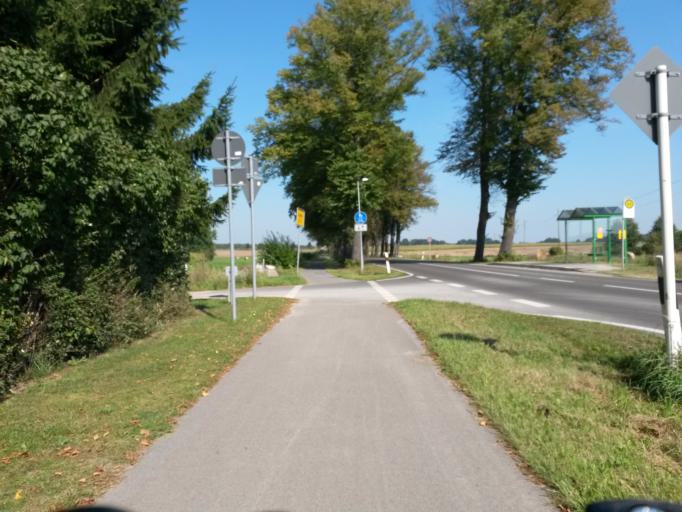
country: DE
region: Brandenburg
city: Templin
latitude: 53.0831
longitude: 13.4466
